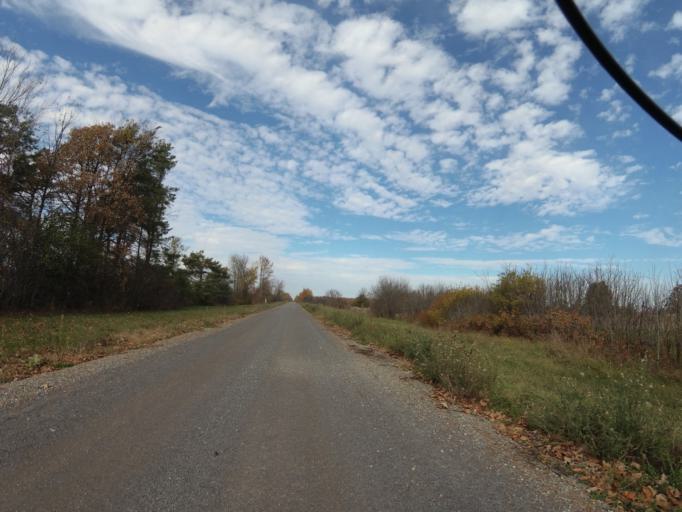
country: CA
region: Ontario
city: Carleton Place
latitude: 45.0450
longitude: -76.0866
